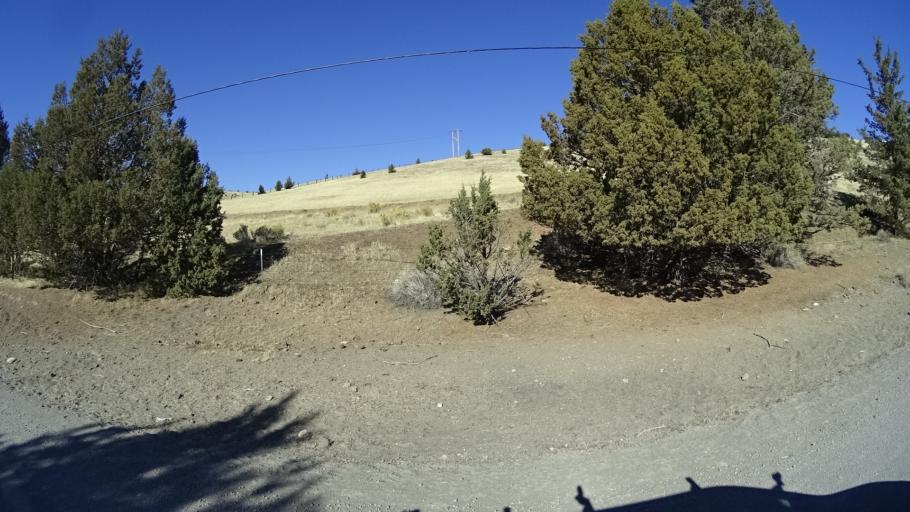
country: US
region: California
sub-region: Siskiyou County
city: Montague
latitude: 41.7303
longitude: -122.3582
